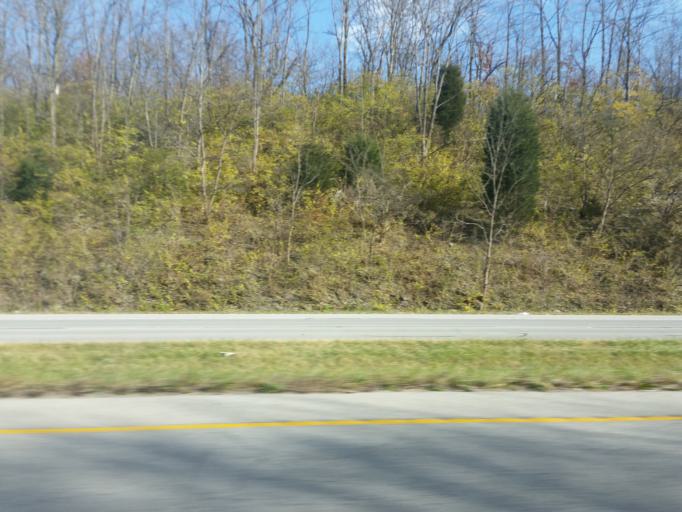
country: US
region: Ohio
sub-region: Hamilton County
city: Dunlap
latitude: 39.2869
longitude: -84.6053
